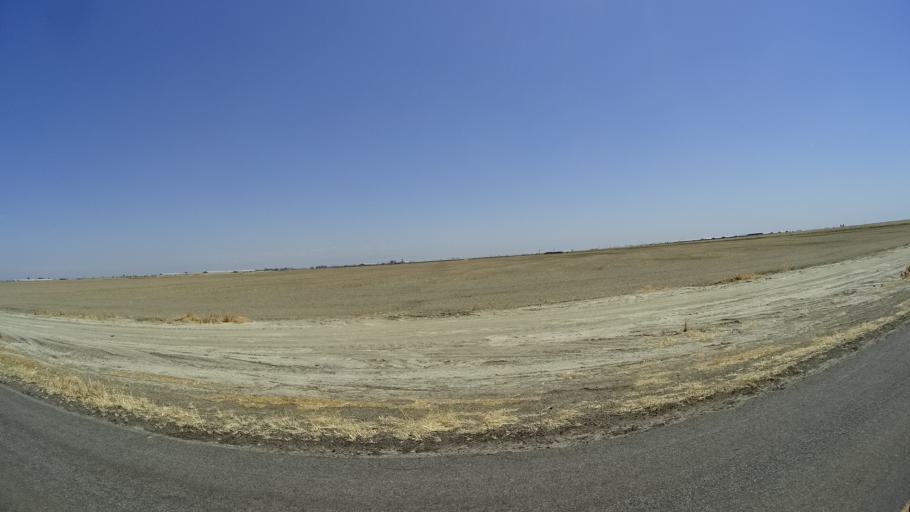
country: US
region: California
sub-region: Kings County
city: Stratford
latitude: 36.1984
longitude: -119.7086
